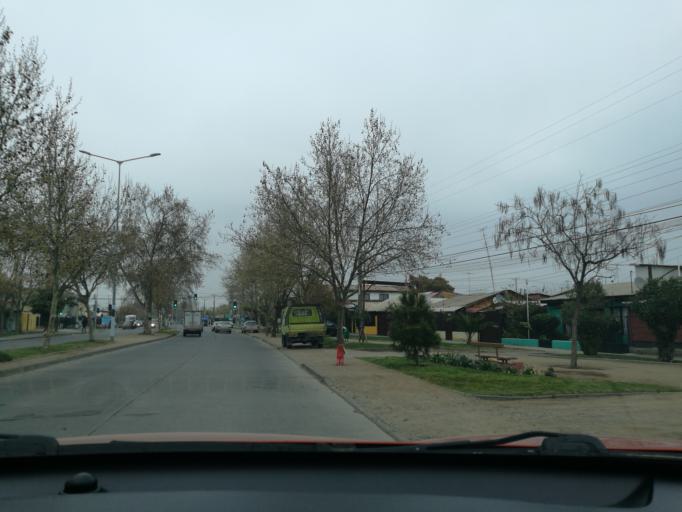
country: CL
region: O'Higgins
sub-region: Provincia de Cachapoal
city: Rancagua
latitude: -34.1620
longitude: -70.7223
